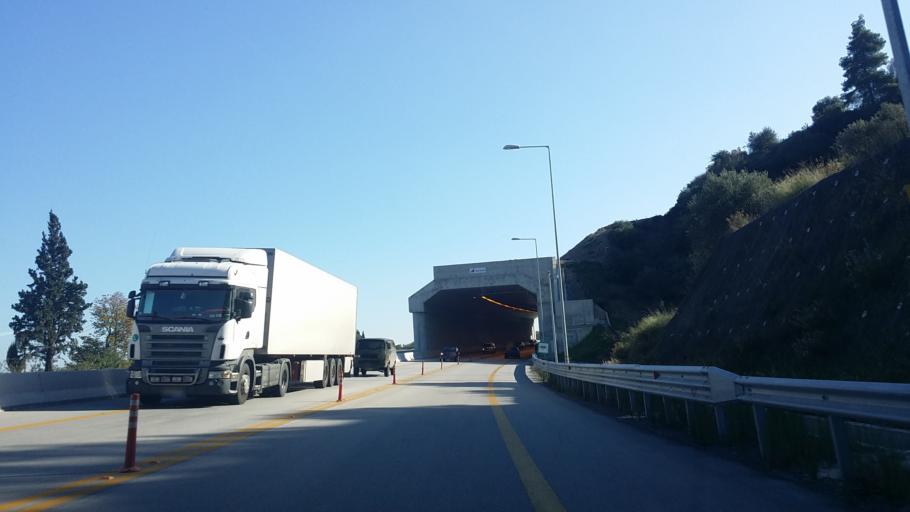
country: GR
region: West Greece
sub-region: Nomos Achaias
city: Temeni
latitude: 38.2086
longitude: 22.1338
